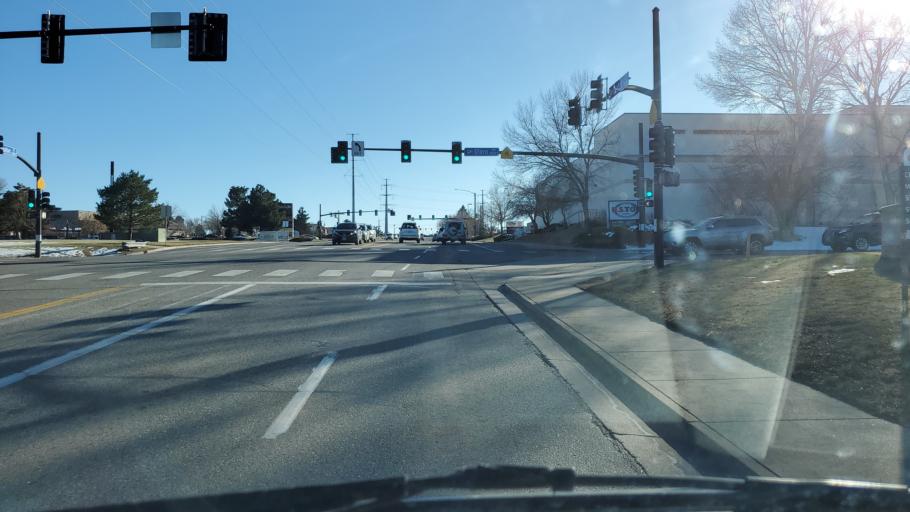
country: US
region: Colorado
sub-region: Arapahoe County
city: Castlewood
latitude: 39.5699
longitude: -104.9045
